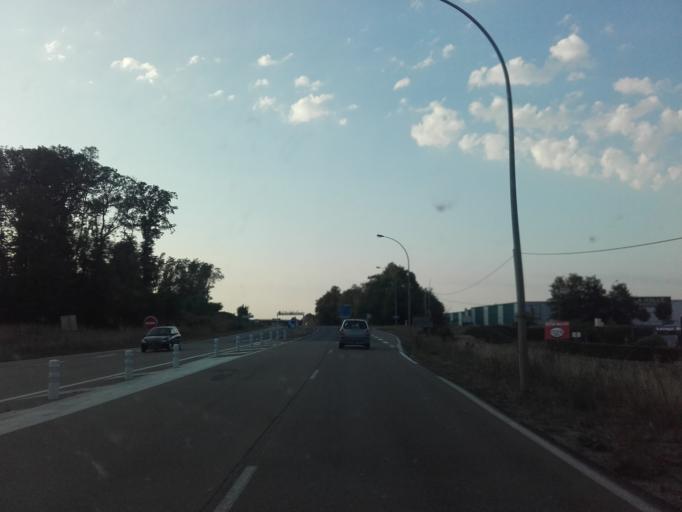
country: FR
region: Bourgogne
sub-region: Departement de l'Yonne
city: Gurgy
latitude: 47.8436
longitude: 3.5506
